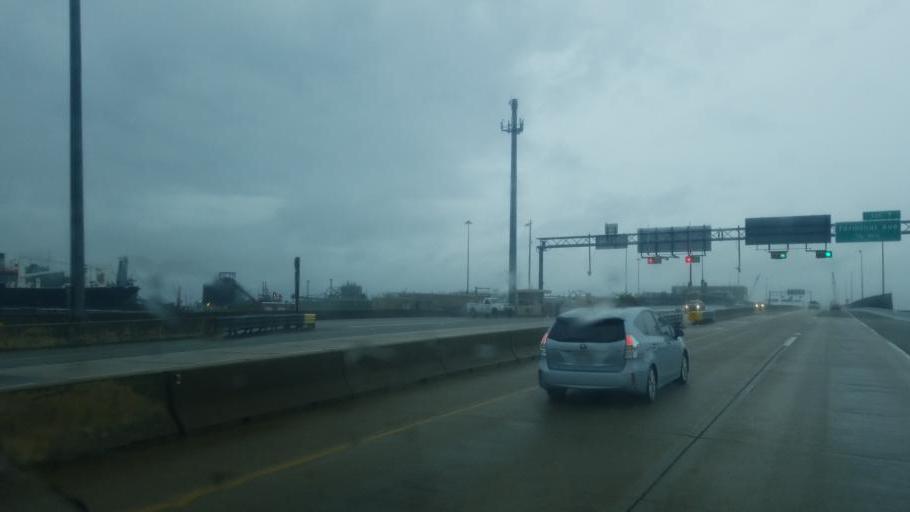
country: US
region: Virginia
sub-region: City of Newport News
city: Newport News
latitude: 36.9618
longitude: -76.4118
